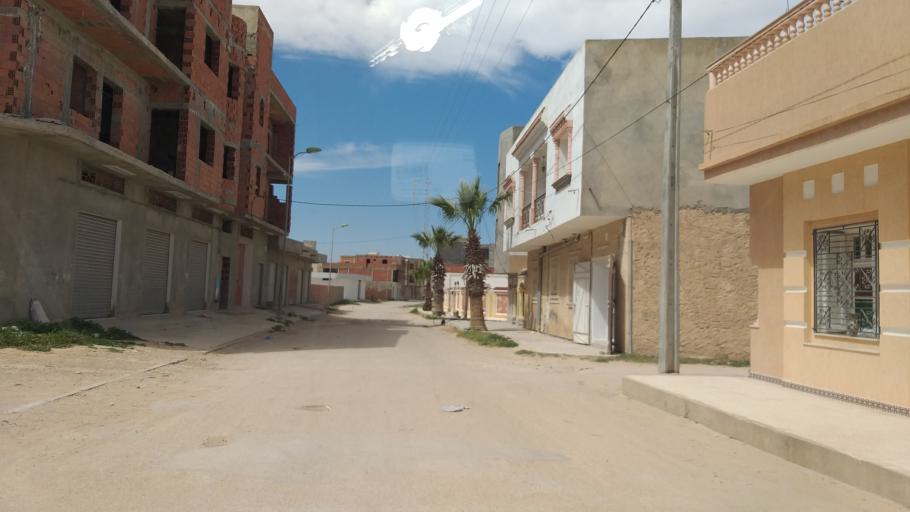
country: TN
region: Al Mahdiyah
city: El Jem
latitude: 35.3016
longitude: 10.6990
